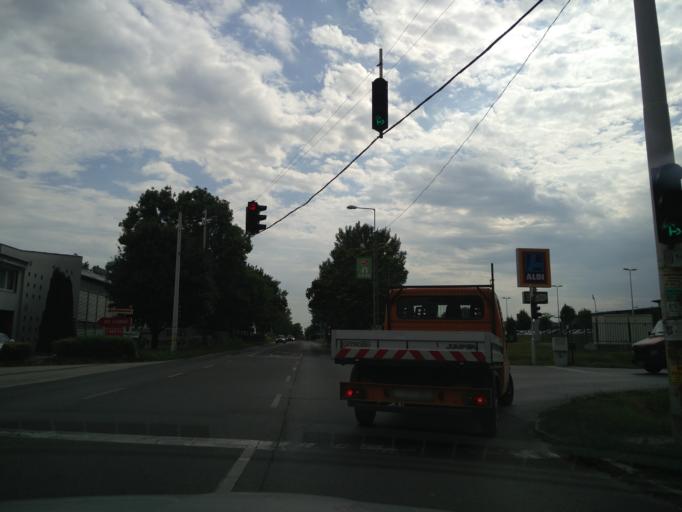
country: HU
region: Pest
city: Budakeszi
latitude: 47.5015
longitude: 18.9196
